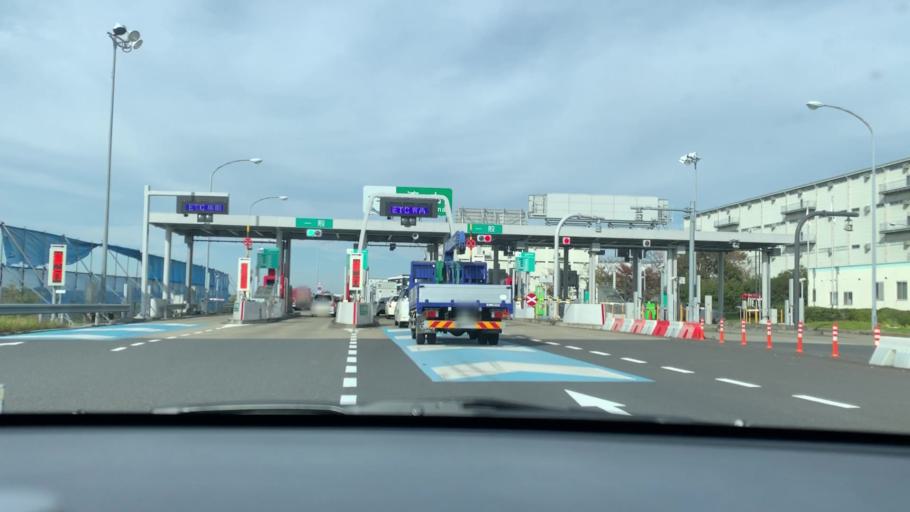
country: JP
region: Chiba
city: Nagareyama
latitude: 35.8793
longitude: 139.8991
